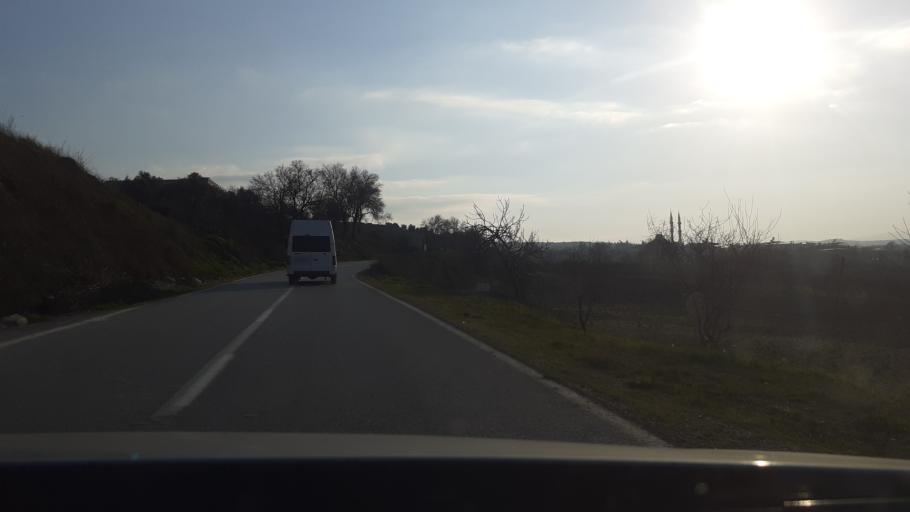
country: TR
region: Hatay
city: Oymakli
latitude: 36.1165
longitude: 36.3034
